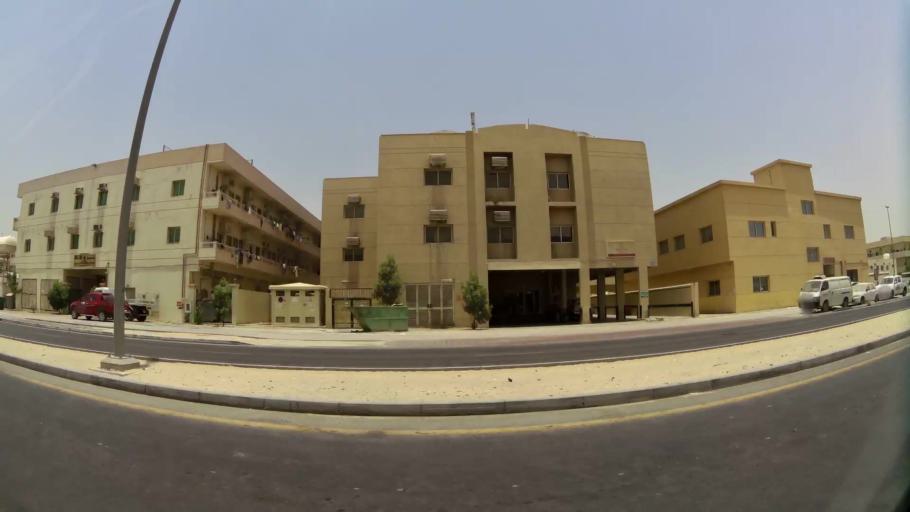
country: AE
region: Ash Shariqah
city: Sharjah
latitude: 25.2718
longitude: 55.4307
